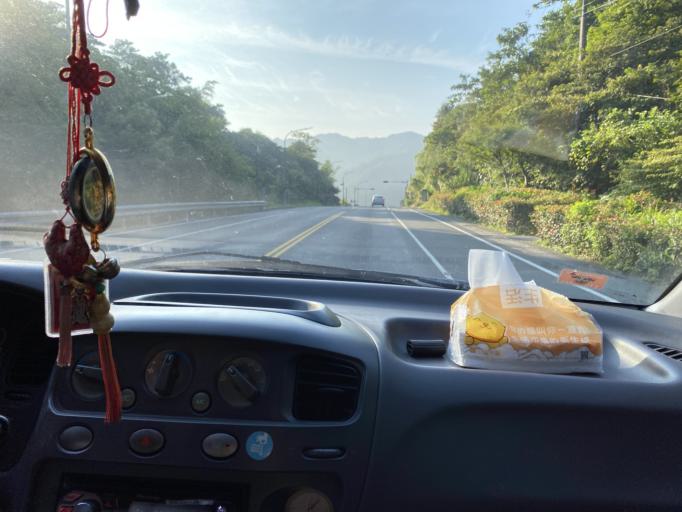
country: TW
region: Taiwan
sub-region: Keelung
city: Keelung
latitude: 25.0495
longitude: 121.7762
